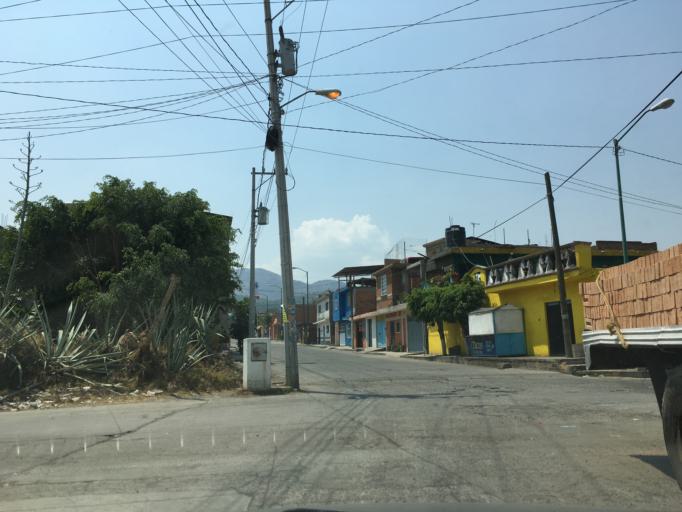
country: MX
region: Michoacan
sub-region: Morelia
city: Morelos
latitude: 19.6428
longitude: -101.2341
